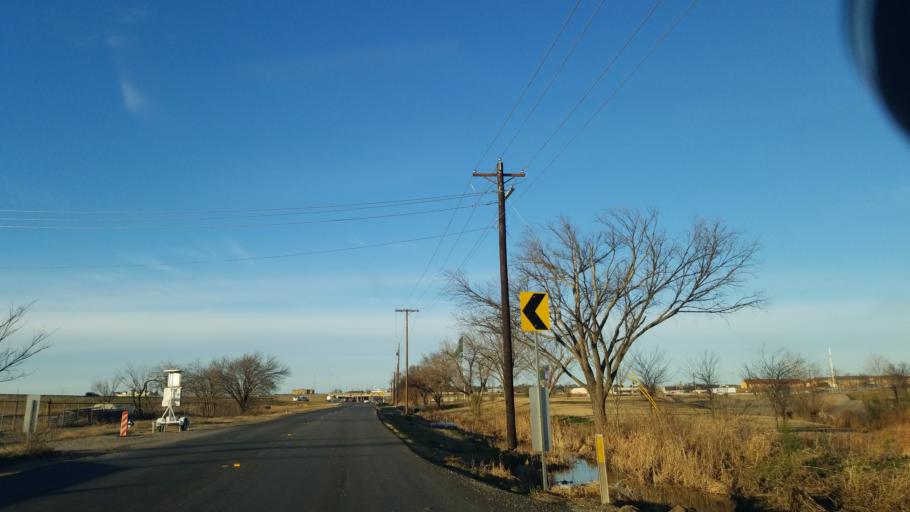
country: US
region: Texas
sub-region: Denton County
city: Denton
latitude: 33.2037
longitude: -97.1615
